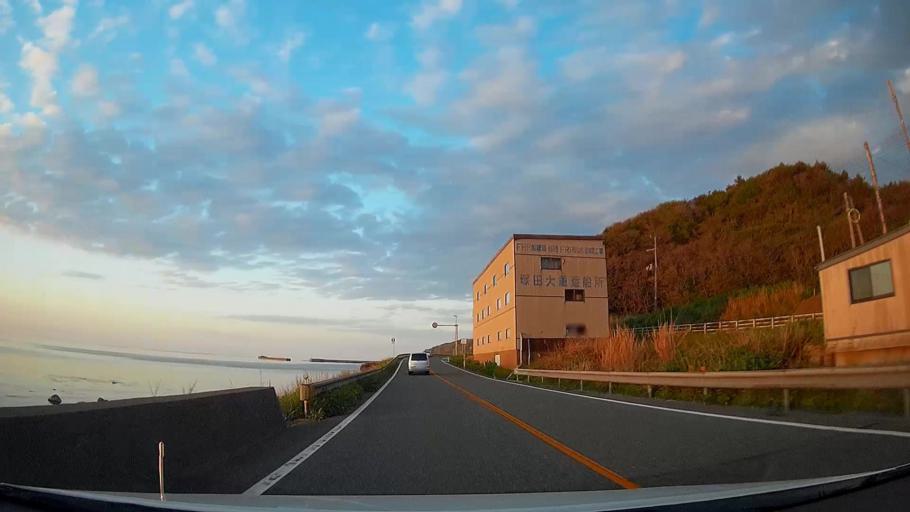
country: JP
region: Niigata
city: Joetsu
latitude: 37.1239
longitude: 138.0417
